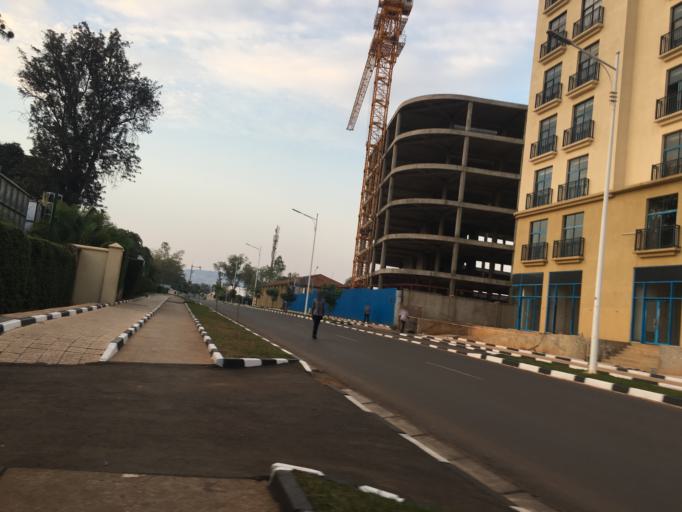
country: RW
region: Kigali
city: Kigali
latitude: -1.9552
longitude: 30.0619
